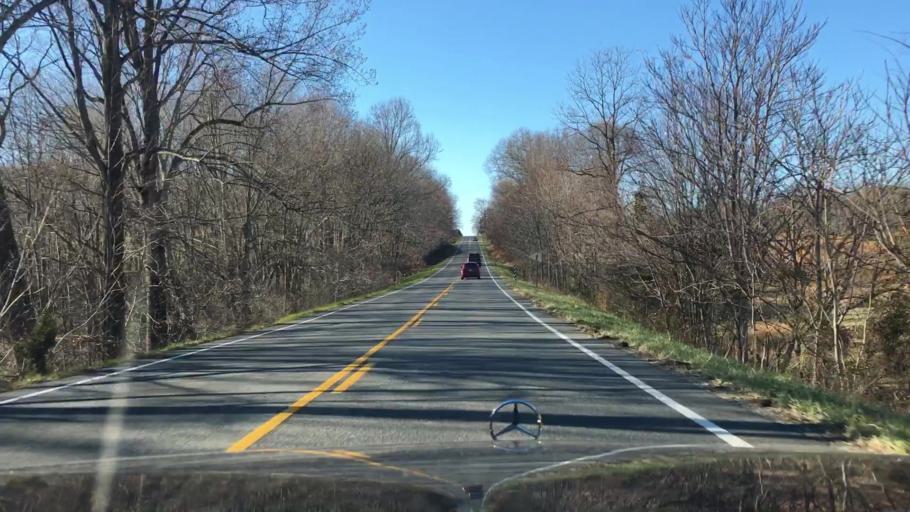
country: US
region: Virginia
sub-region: Franklin County
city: North Shore
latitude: 37.2407
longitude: -79.6632
